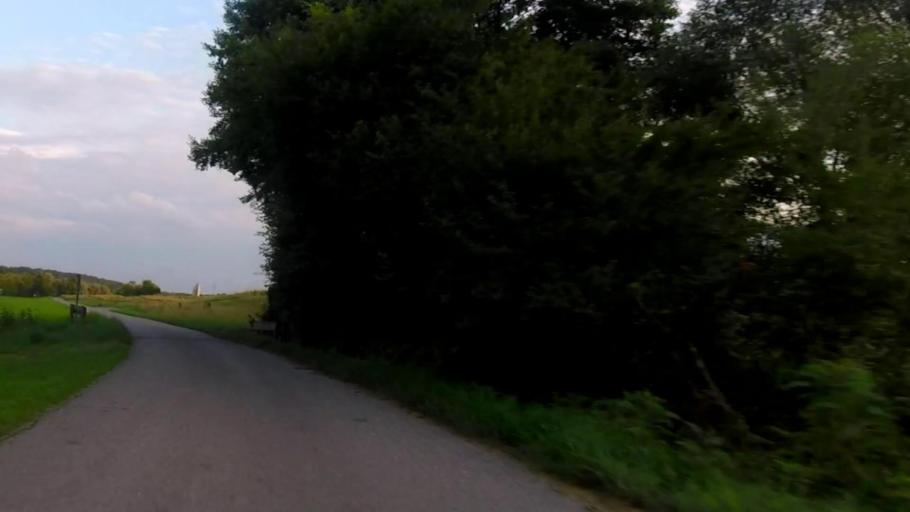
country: DE
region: Baden-Wuerttemberg
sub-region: Regierungsbezirk Stuttgart
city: Aspach
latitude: 48.9688
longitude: 9.3745
